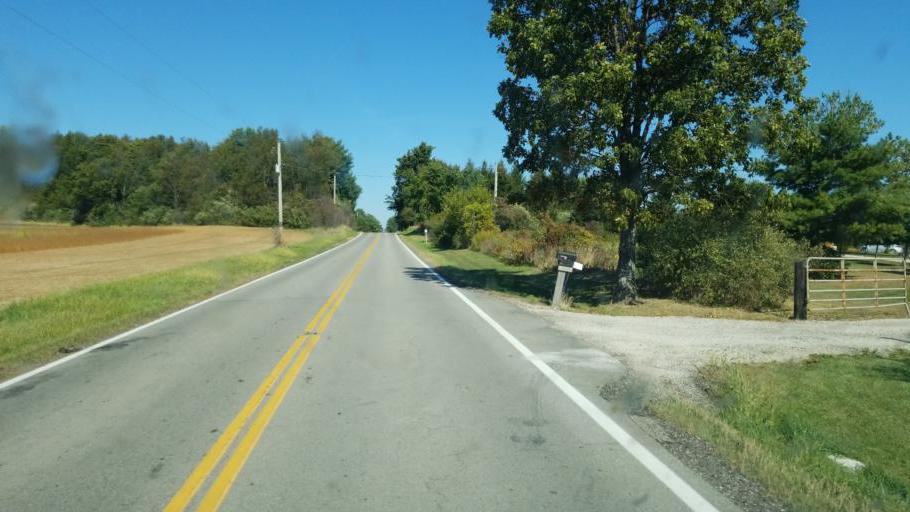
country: US
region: Ohio
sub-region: Huron County
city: Plymouth
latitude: 40.9831
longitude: -82.7085
